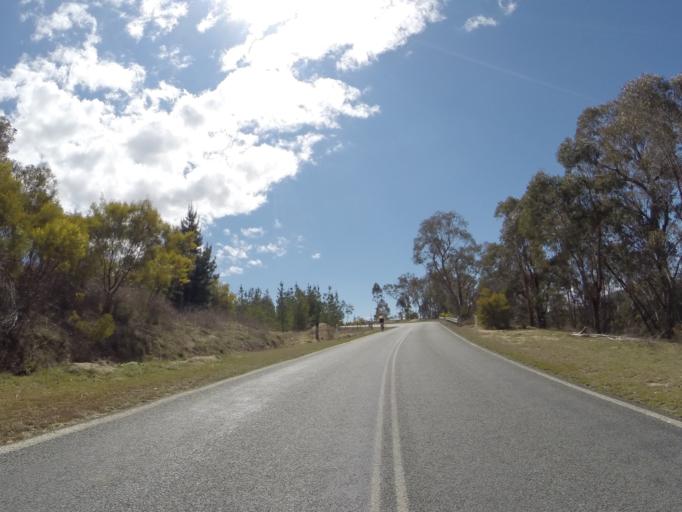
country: AU
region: Australian Capital Territory
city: Macquarie
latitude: -35.3618
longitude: 148.9508
